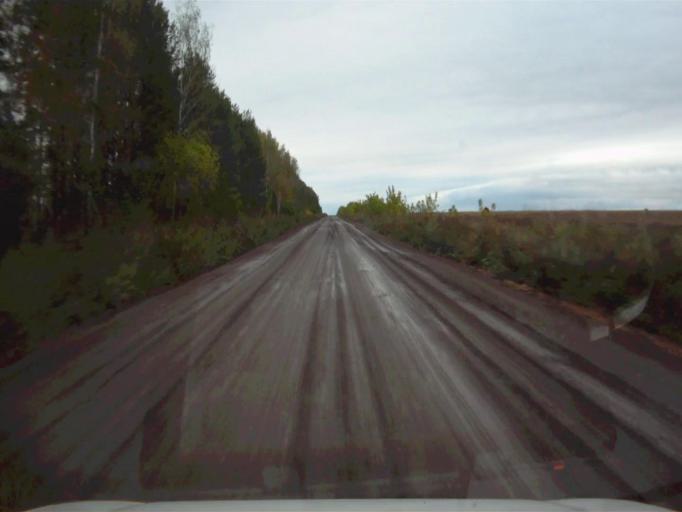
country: RU
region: Sverdlovsk
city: Mikhaylovsk
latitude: 56.1527
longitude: 59.2653
